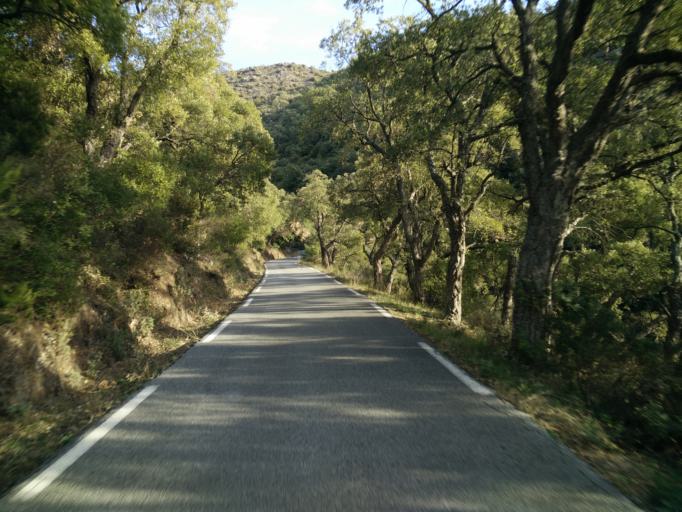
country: FR
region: Provence-Alpes-Cote d'Azur
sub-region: Departement du Var
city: Collobrieres
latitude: 43.1991
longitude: 6.3140
